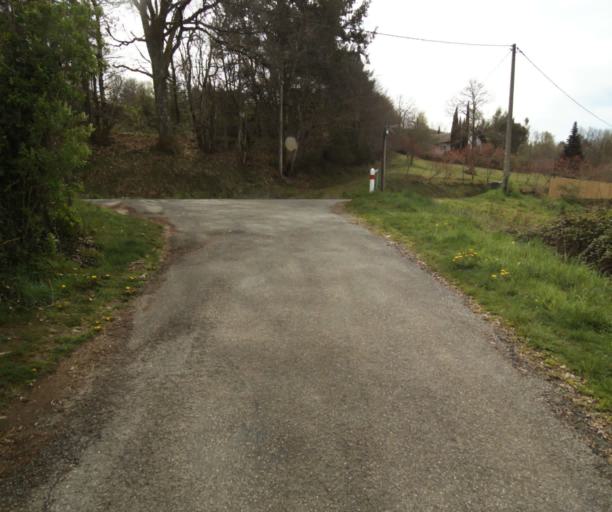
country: FR
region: Limousin
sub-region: Departement de la Correze
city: Laguenne
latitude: 45.2405
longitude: 1.8627
